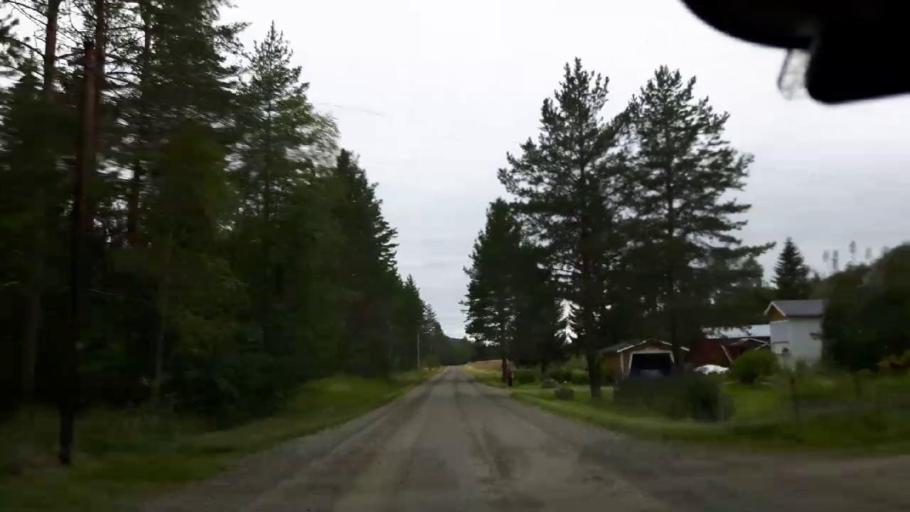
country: SE
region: Vaesternorrland
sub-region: Ange Kommun
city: Fransta
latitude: 62.7876
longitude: 16.0585
